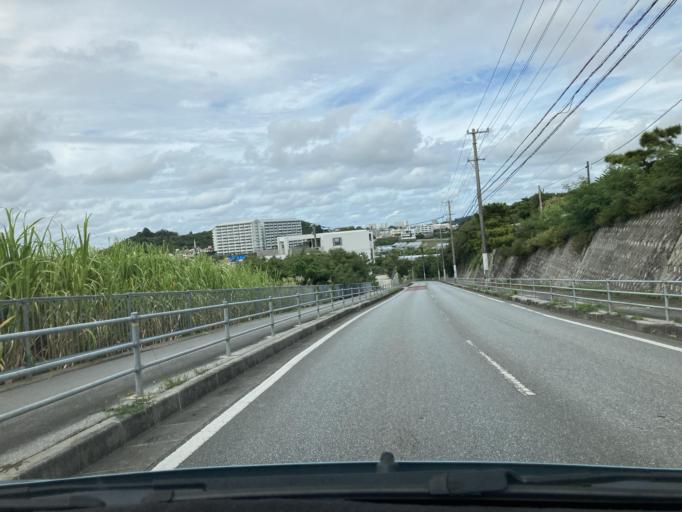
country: JP
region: Okinawa
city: Tomigusuku
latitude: 26.1619
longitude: 127.6798
